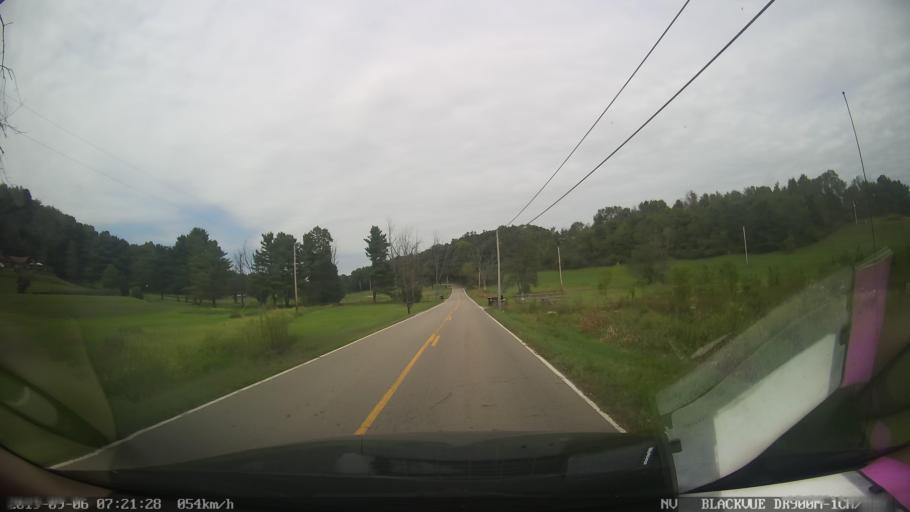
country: US
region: Ohio
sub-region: Licking County
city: Newark
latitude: 40.1330
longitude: -82.3759
